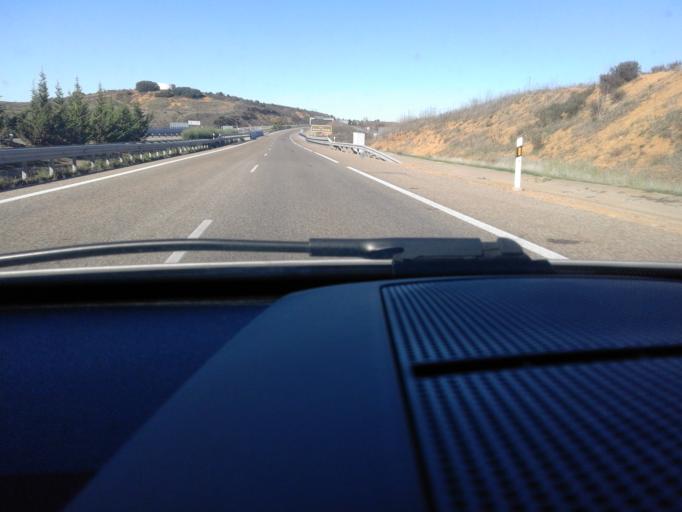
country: ES
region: Castille and Leon
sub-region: Provincia de Leon
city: Onzonilla
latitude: 42.5475
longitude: -5.6202
